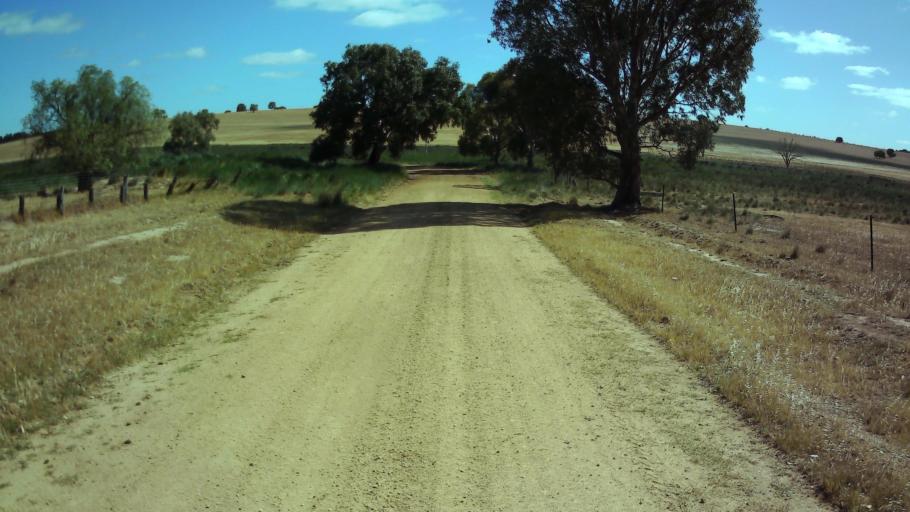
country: AU
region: New South Wales
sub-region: Weddin
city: Grenfell
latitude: -33.9807
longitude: 148.3912
